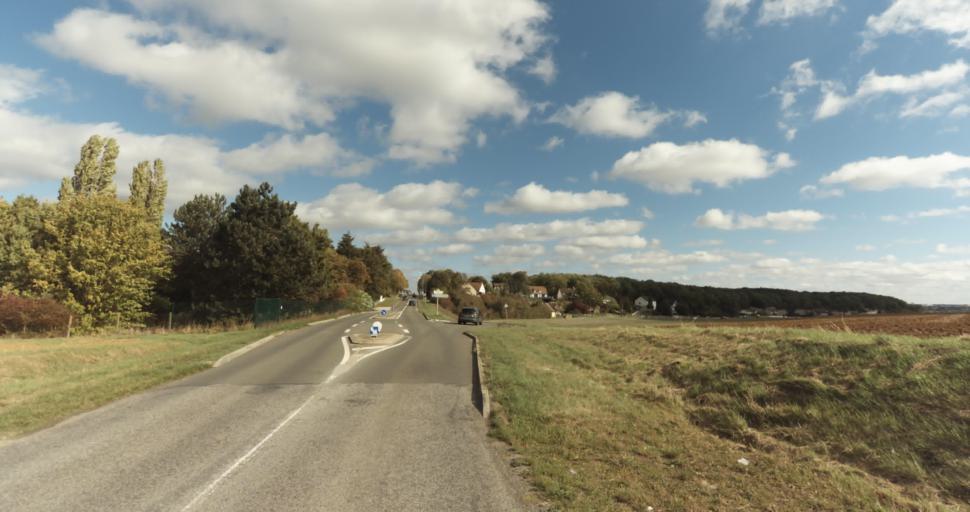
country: FR
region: Centre
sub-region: Departement d'Eure-et-Loir
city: Garnay
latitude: 48.7210
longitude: 1.3233
